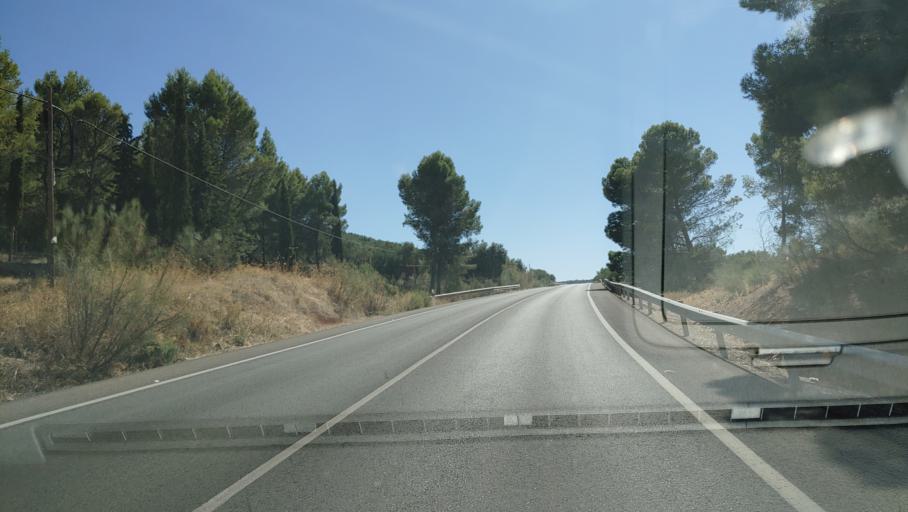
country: ES
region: Andalusia
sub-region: Provincia de Jaen
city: Campina
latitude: 38.2505
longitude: -2.9624
